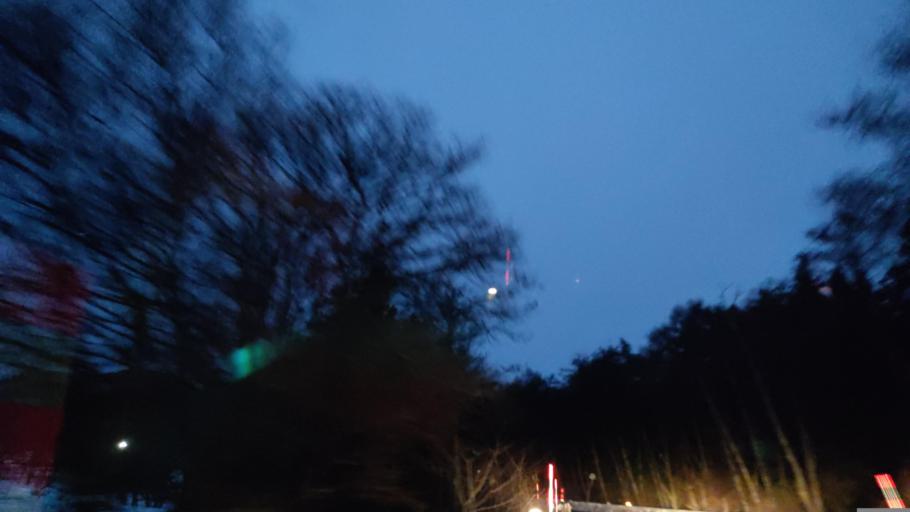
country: JP
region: Iwate
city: Morioka-shi
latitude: 39.6338
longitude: 141.0966
